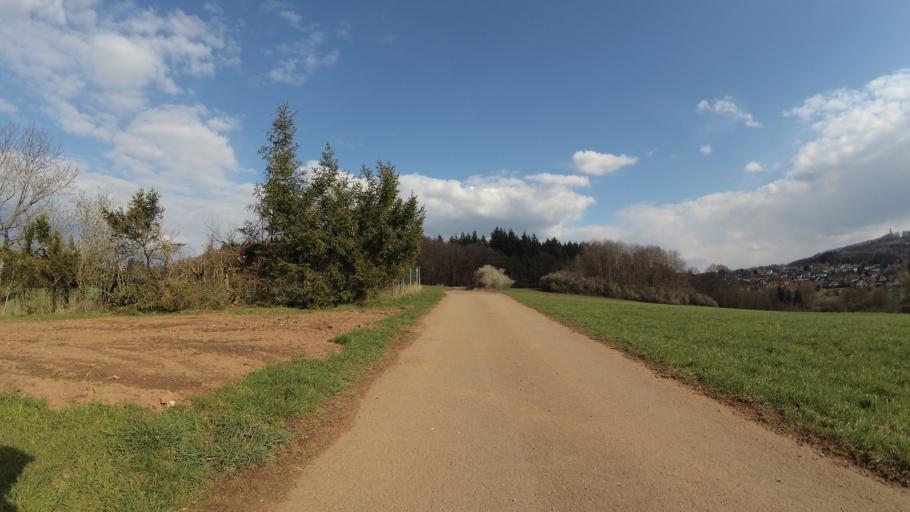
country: DE
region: Saarland
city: Tholey
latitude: 49.5100
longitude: 7.0287
